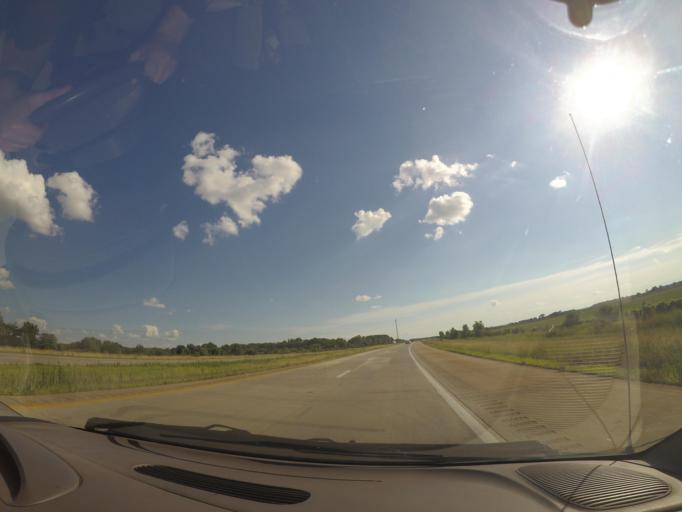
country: US
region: Ohio
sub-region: Lucas County
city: Whitehouse
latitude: 41.4689
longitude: -83.7780
